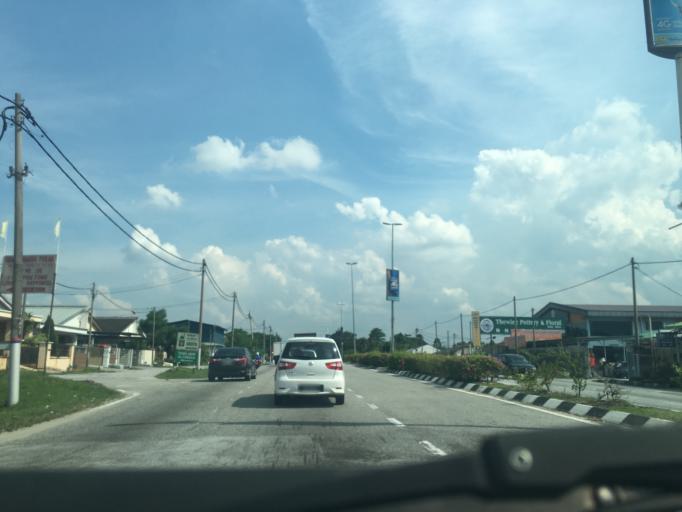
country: MY
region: Perak
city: Ipoh
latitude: 4.6186
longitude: 101.0802
